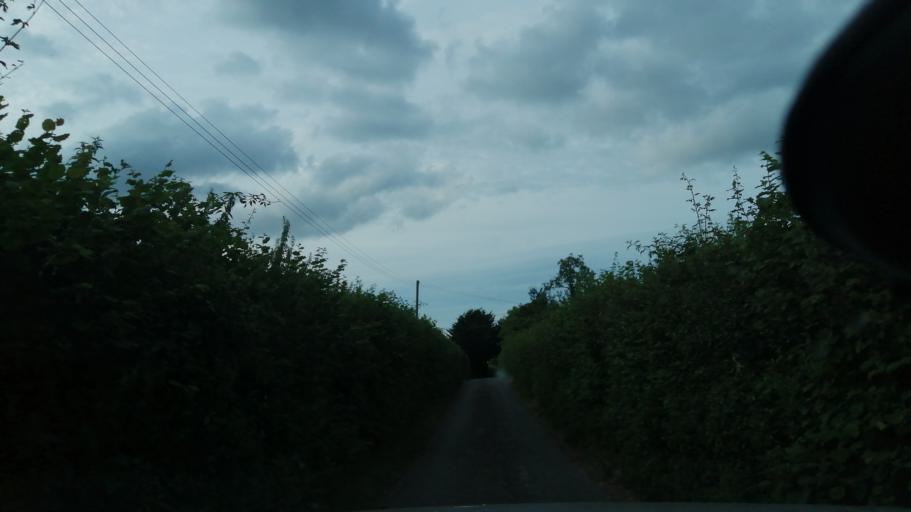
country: GB
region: England
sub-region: Herefordshire
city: Thruxton
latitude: 52.0084
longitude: -2.8028
